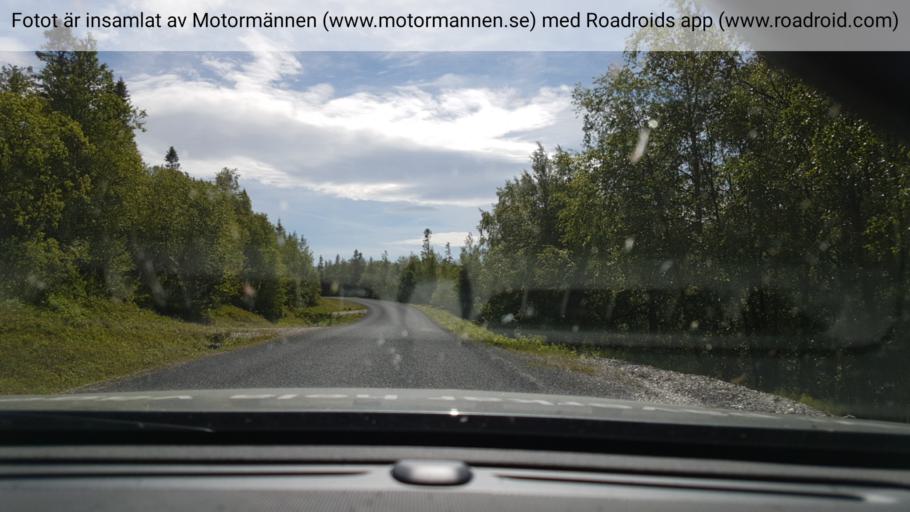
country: SE
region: Vaesterbotten
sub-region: Vilhelmina Kommun
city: Sjoberg
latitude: 65.2841
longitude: 15.2969
